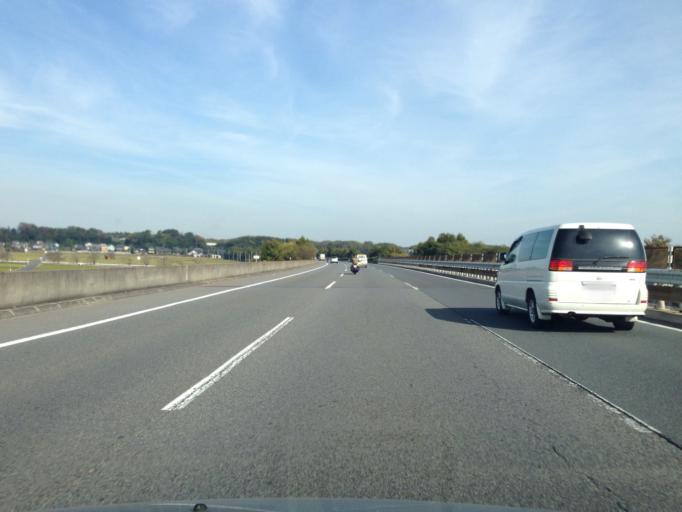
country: JP
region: Ibaraki
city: Naka
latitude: 36.0971
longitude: 140.1685
